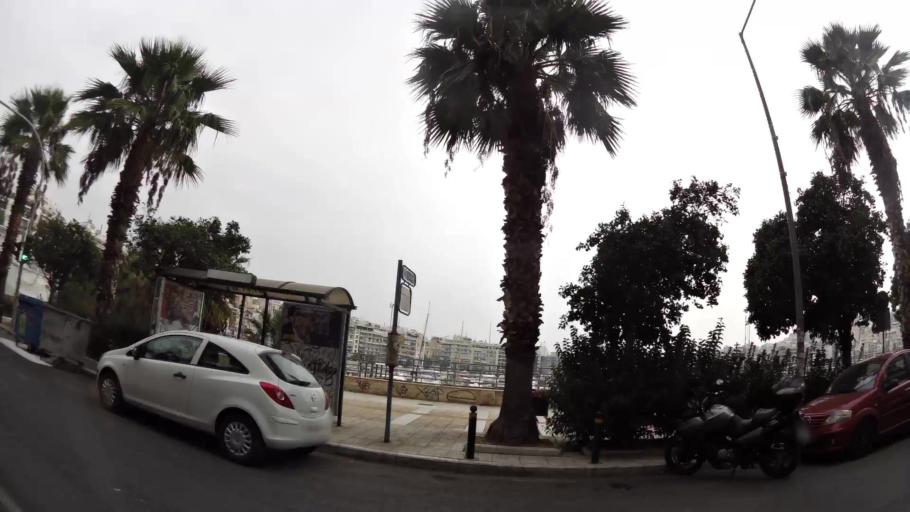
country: GR
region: Attica
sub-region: Nomos Attikis
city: Piraeus
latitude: 37.9358
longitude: 23.6467
